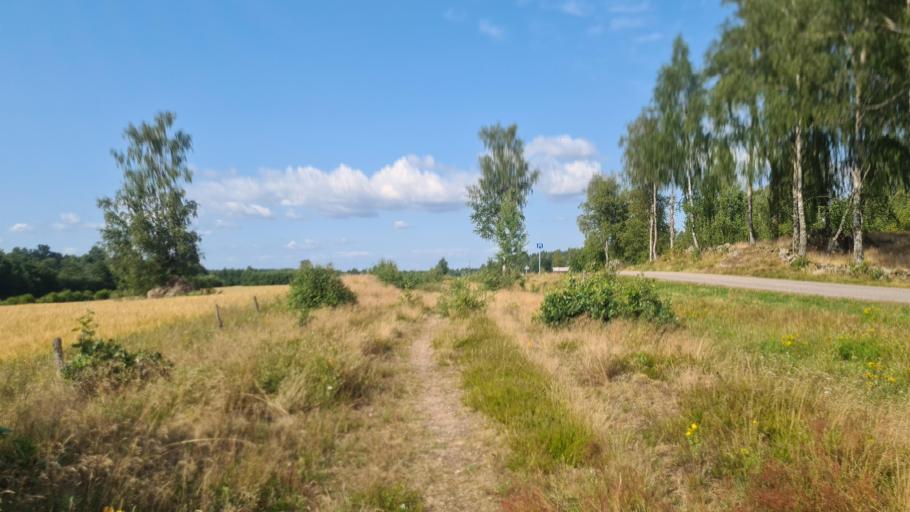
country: SE
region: Kronoberg
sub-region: Ljungby Kommun
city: Ljungby
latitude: 56.7480
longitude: 13.8809
